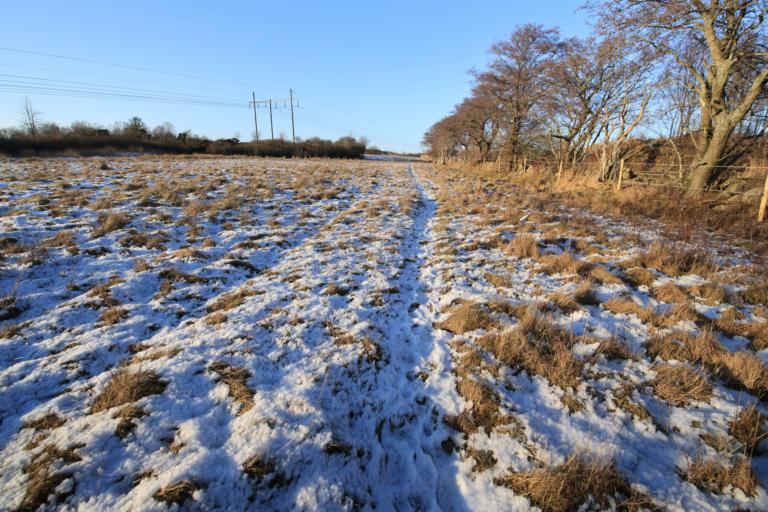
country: SE
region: Halland
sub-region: Varbergs Kommun
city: Varberg
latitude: 57.1292
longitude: 12.3030
